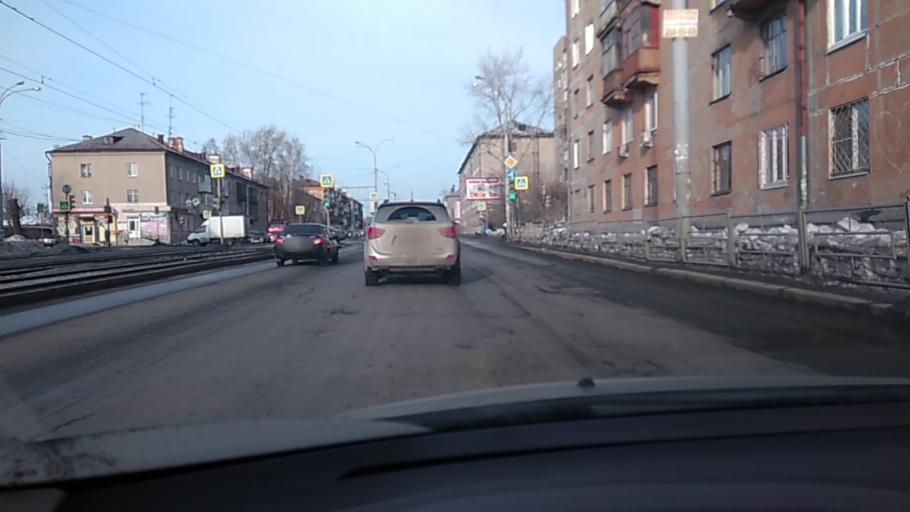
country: RU
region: Sverdlovsk
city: Yekaterinburg
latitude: 56.8849
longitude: 60.5635
